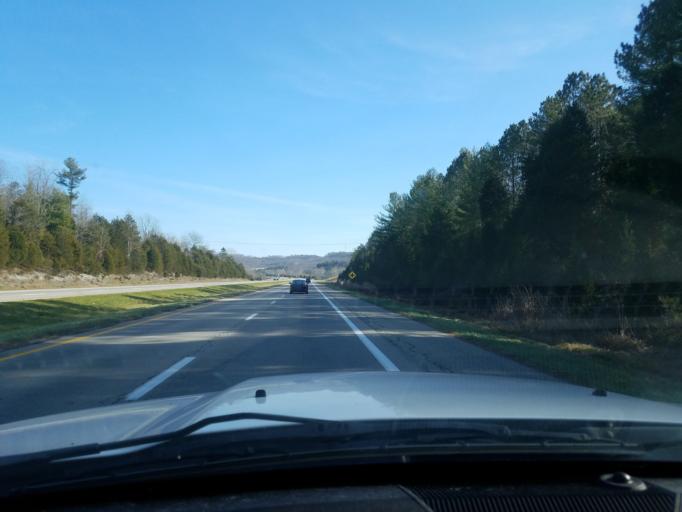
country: US
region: Ohio
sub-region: Adams County
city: Peebles
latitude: 38.9336
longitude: -83.4801
